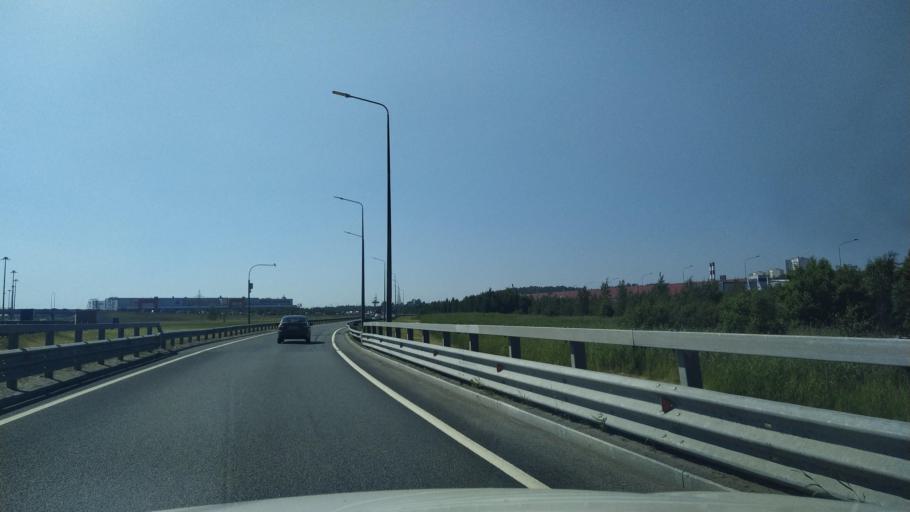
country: RU
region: St.-Petersburg
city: Pargolovo
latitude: 60.0994
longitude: 30.2760
